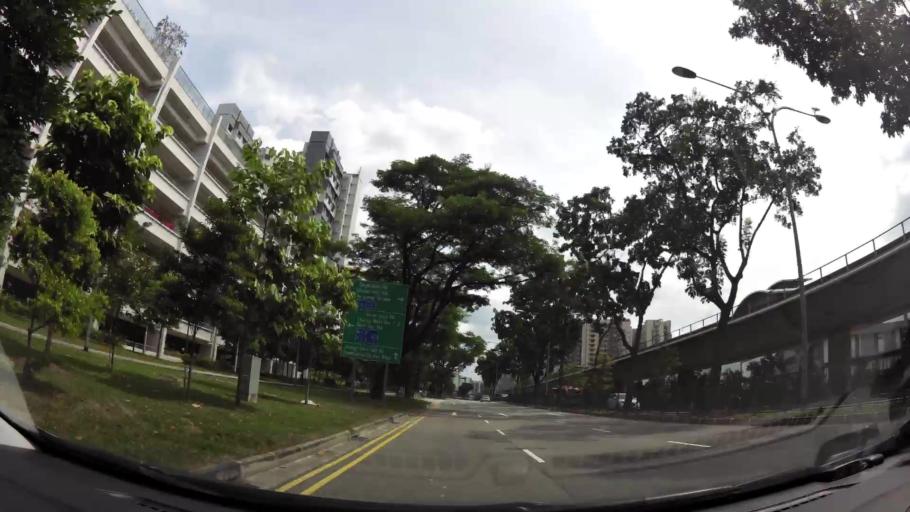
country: MY
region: Johor
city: Johor Bahru
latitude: 1.3422
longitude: 103.7137
